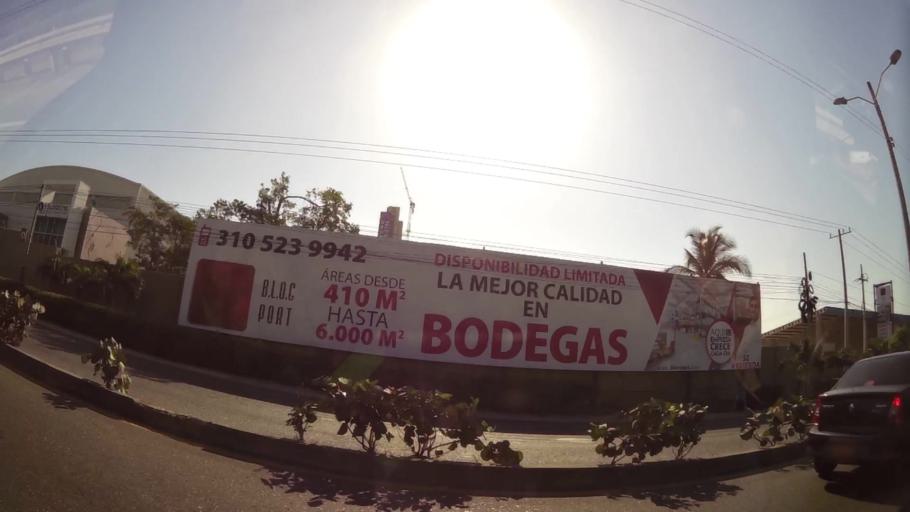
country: CO
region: Bolivar
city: Cartagena
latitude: 10.3777
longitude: -75.5036
